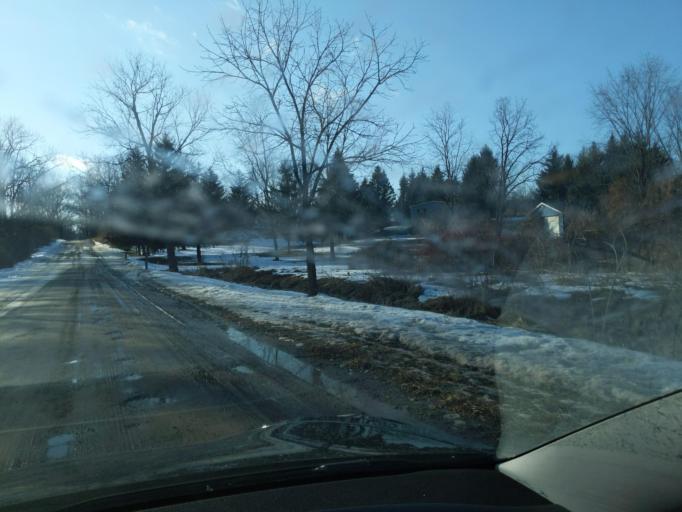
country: US
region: Michigan
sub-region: Ingham County
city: Stockbridge
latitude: 42.5244
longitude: -84.1081
